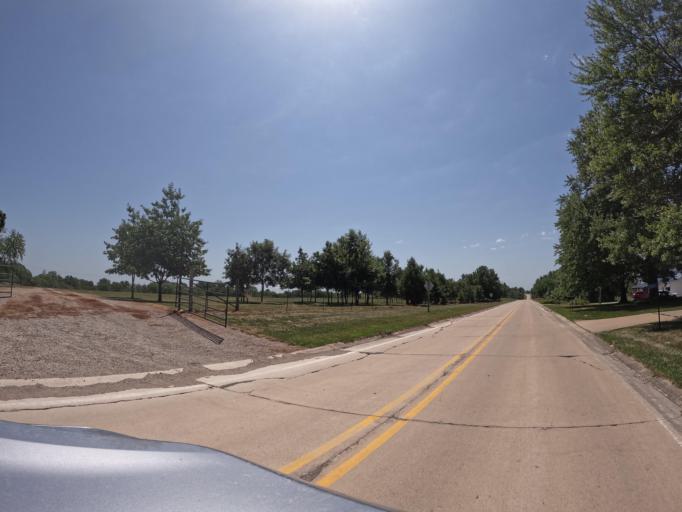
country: US
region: Iowa
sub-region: Henry County
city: Mount Pleasant
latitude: 40.9536
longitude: -91.5545
